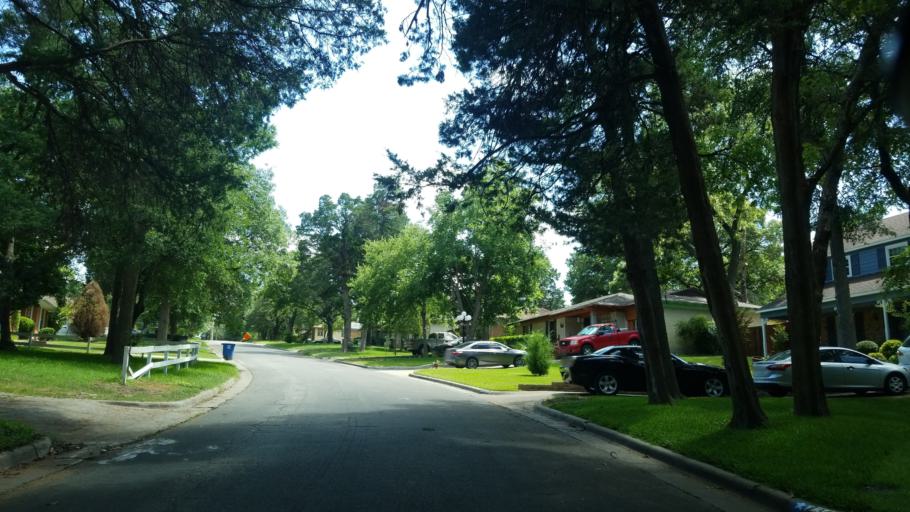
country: US
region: Texas
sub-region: Dallas County
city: Balch Springs
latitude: 32.7549
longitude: -96.6982
